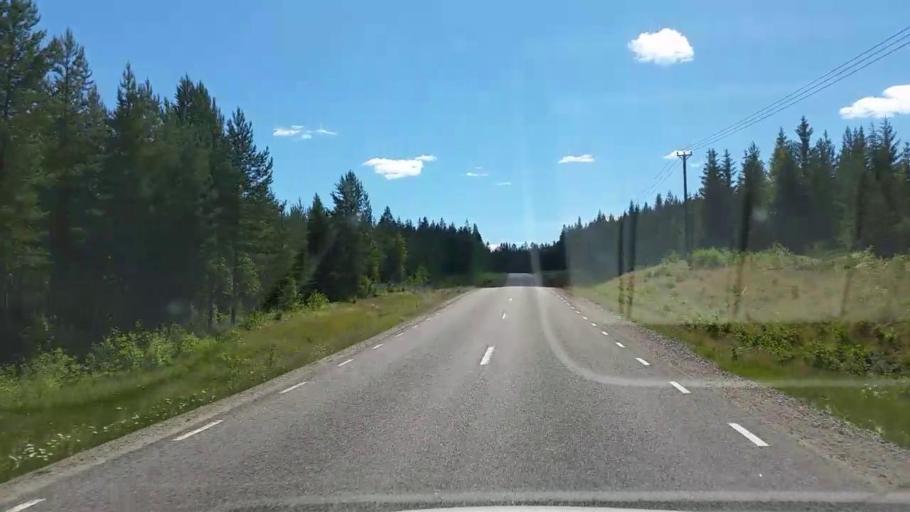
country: SE
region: Gaevleborg
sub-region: Ovanakers Kommun
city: Edsbyn
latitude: 61.5339
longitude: 15.6797
